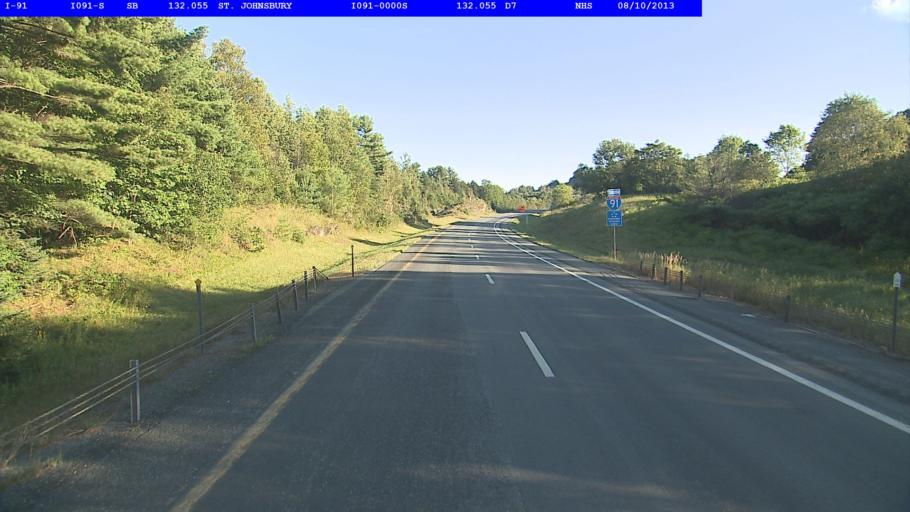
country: US
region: Vermont
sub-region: Caledonia County
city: St Johnsbury
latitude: 44.4463
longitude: -72.0246
